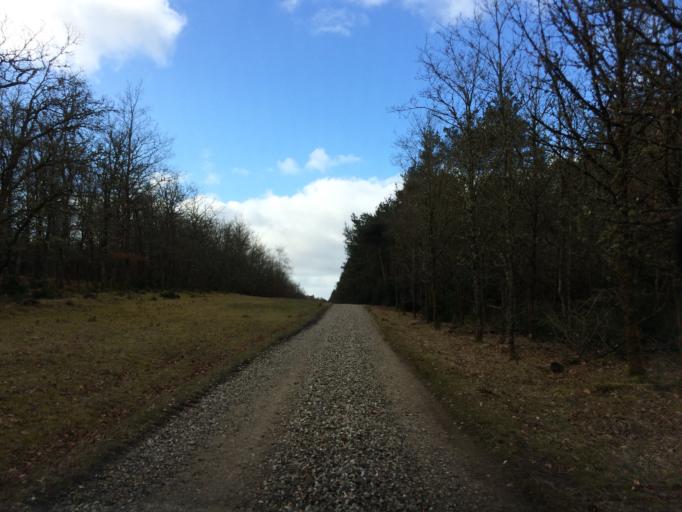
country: DK
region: Central Jutland
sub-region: Holstebro Kommune
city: Ulfborg
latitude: 56.2693
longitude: 8.4512
